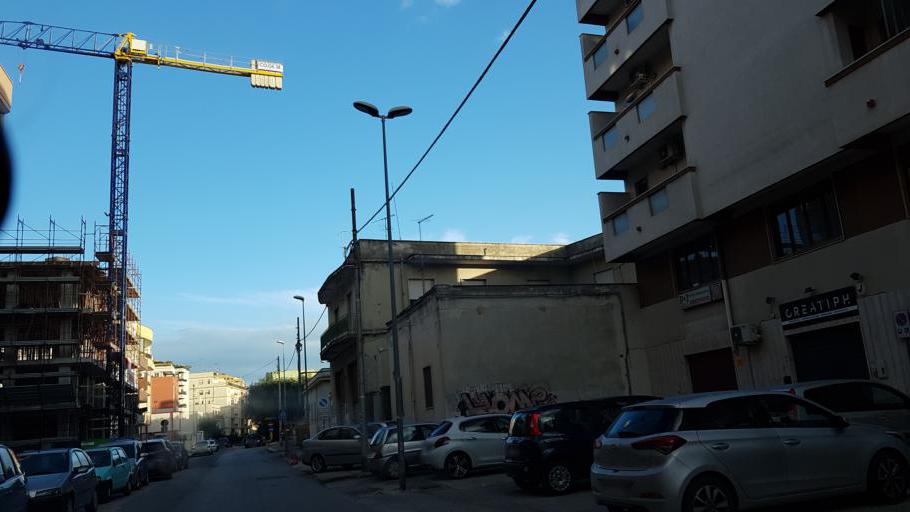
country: IT
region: Apulia
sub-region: Provincia di Brindisi
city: Brindisi
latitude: 40.6370
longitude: 17.9331
